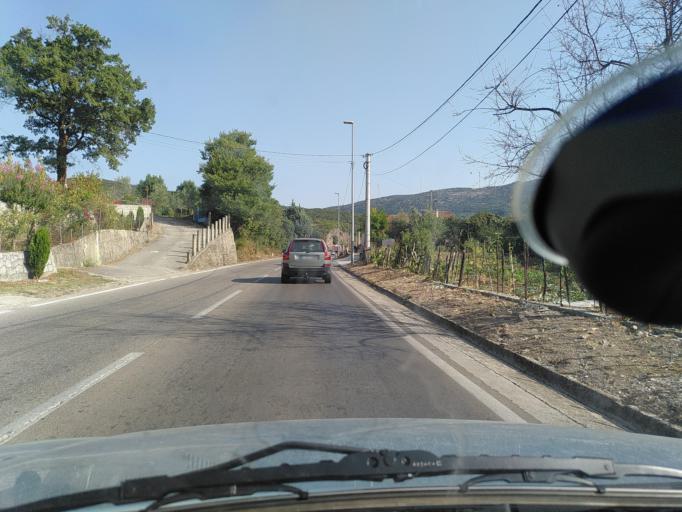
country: ME
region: Ulcinj
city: Ulcinj
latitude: 41.9551
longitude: 19.1912
